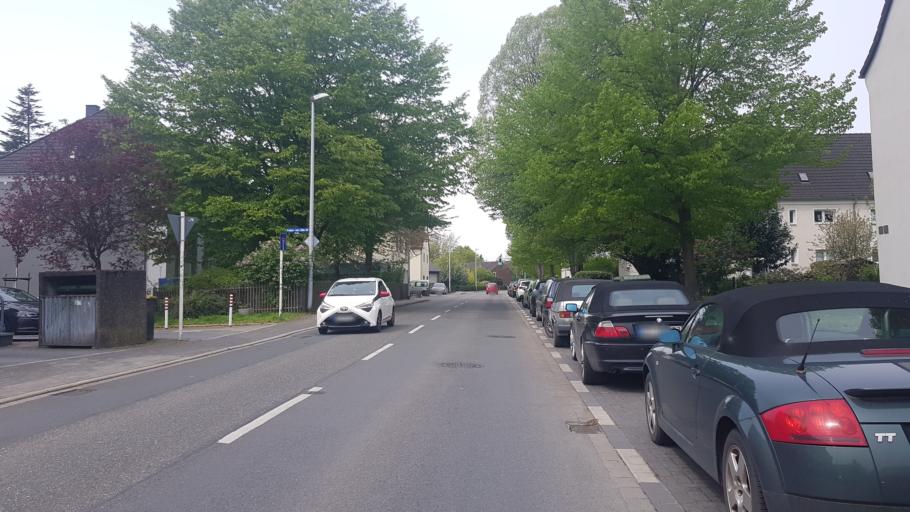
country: DE
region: North Rhine-Westphalia
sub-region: Regierungsbezirk Dusseldorf
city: Muelheim (Ruhr)
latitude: 51.4466
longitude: 6.9169
